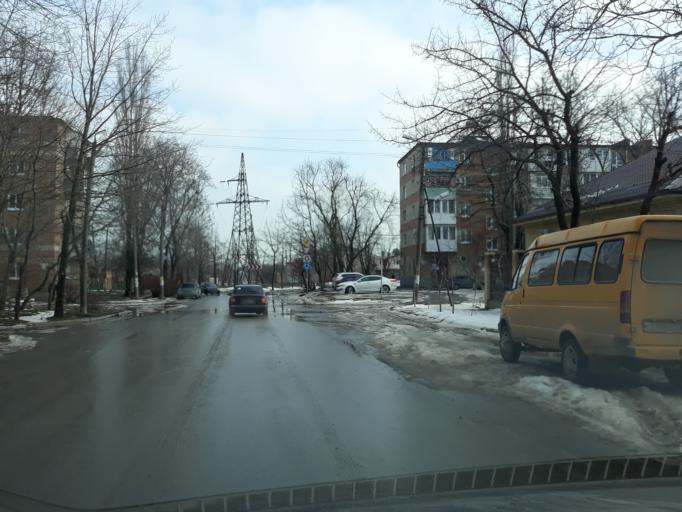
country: RU
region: Rostov
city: Taganrog
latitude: 47.2183
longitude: 38.8903
